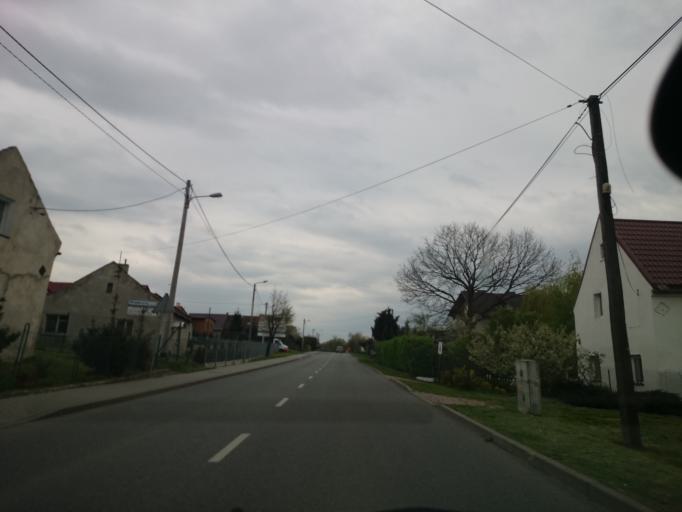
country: PL
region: Opole Voivodeship
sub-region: Powiat nyski
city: Nysa
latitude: 50.4325
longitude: 17.3409
